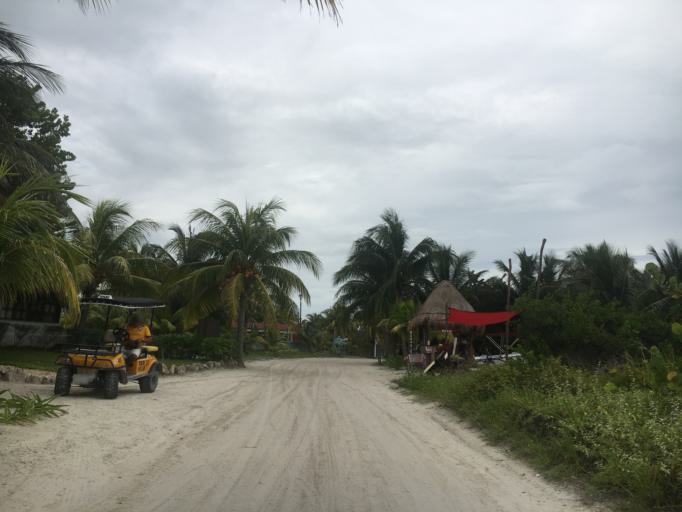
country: MX
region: Quintana Roo
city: Kantunilkin
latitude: 21.5272
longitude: -87.3758
